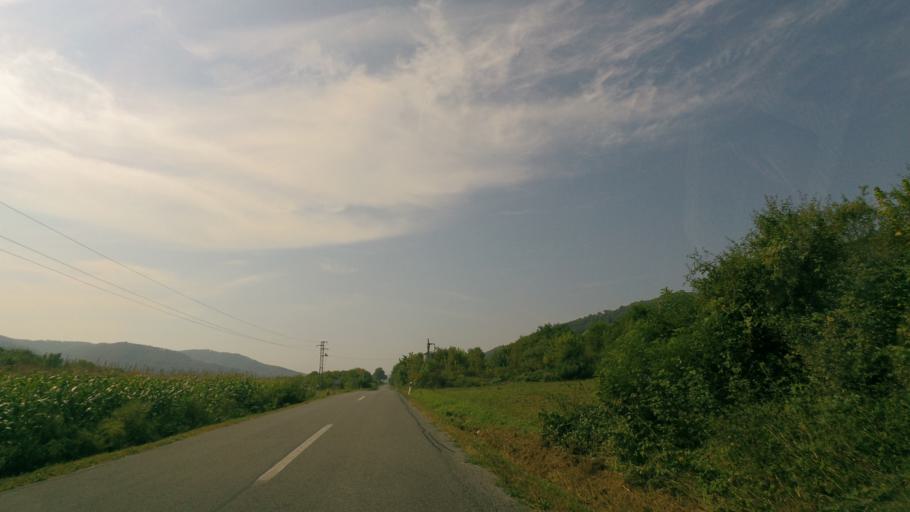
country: BA
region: Republika Srpska
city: Kostajnica
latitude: 45.2051
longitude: 16.4883
